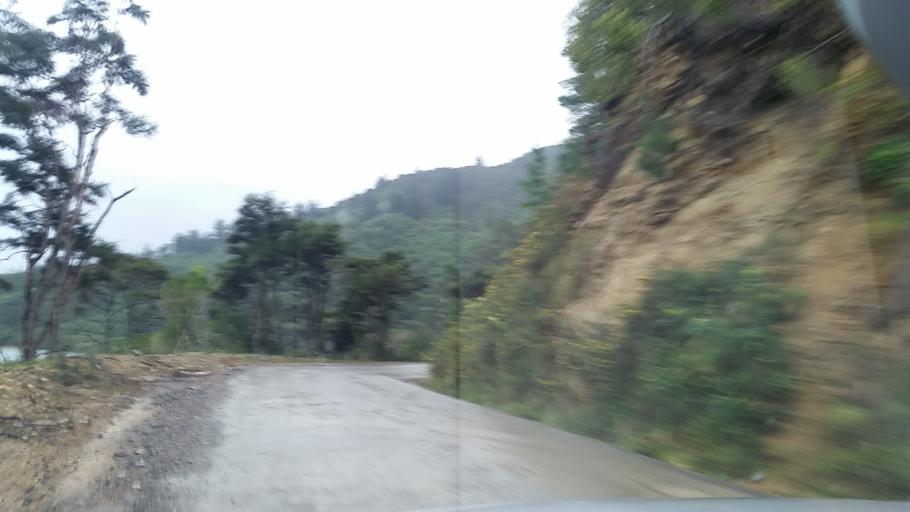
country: NZ
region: Marlborough
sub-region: Marlborough District
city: Picton
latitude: -41.1775
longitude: 174.0624
